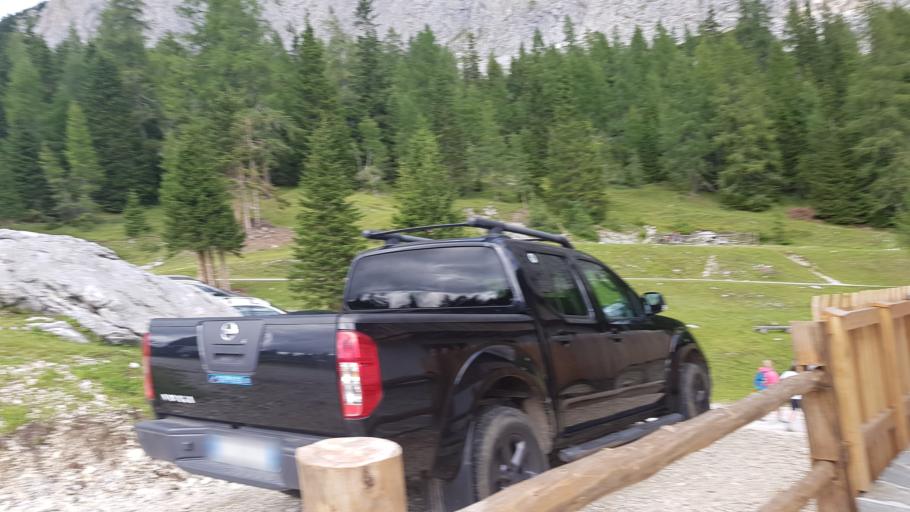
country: IT
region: Veneto
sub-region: Provincia di Belluno
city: Granvilla
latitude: 46.6234
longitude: 12.7097
